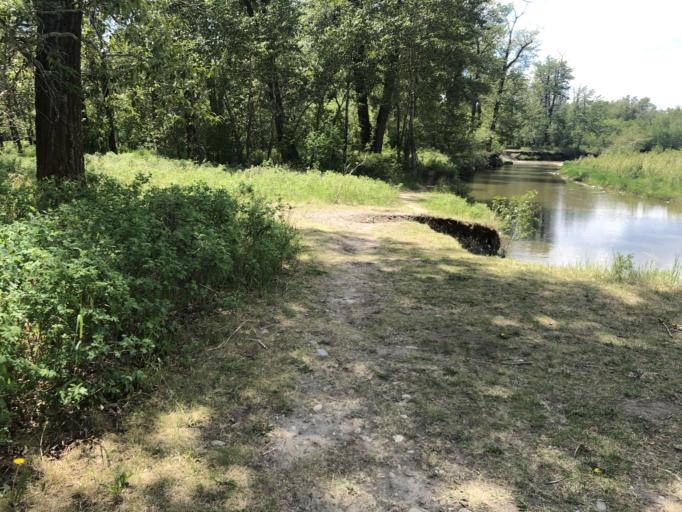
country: CA
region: Alberta
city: Calgary
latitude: 50.9285
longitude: -114.0598
